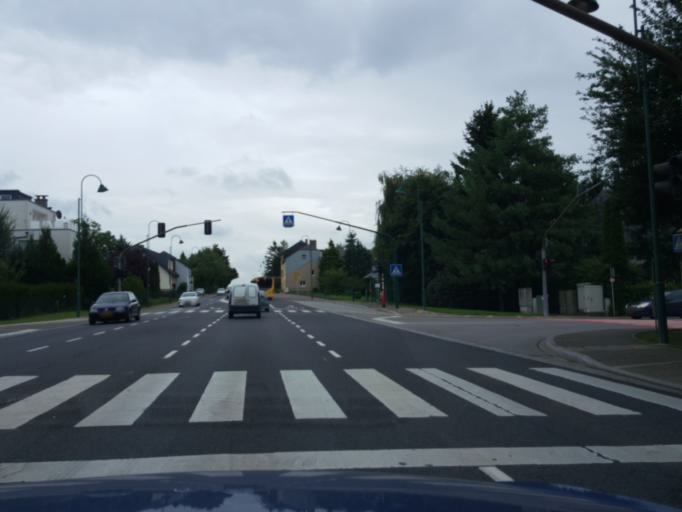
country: LU
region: Luxembourg
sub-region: Canton de Capellen
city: Mamer
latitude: 49.6342
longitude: 6.0164
